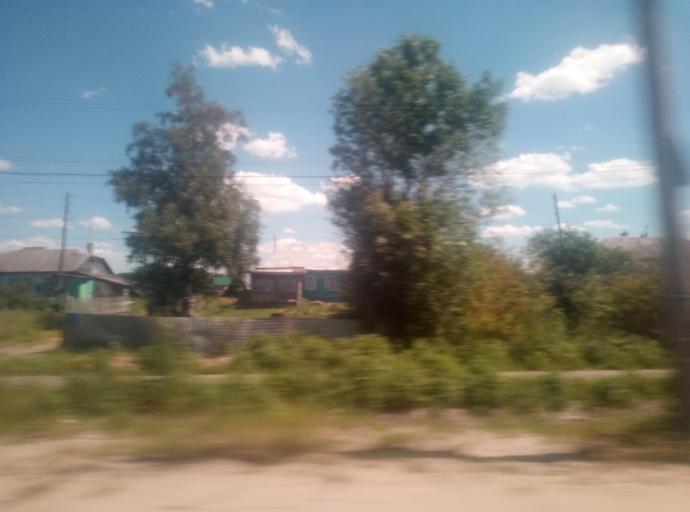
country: RU
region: Tula
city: Kireyevsk
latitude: 53.9839
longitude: 37.9331
